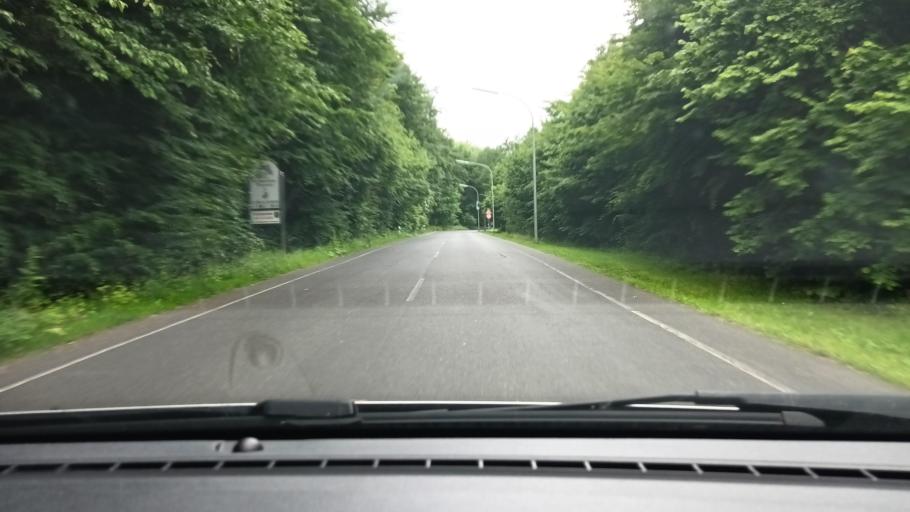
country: DE
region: North Rhine-Westphalia
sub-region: Regierungsbezirk Koln
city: Hurth
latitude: 50.8550
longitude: 6.8785
